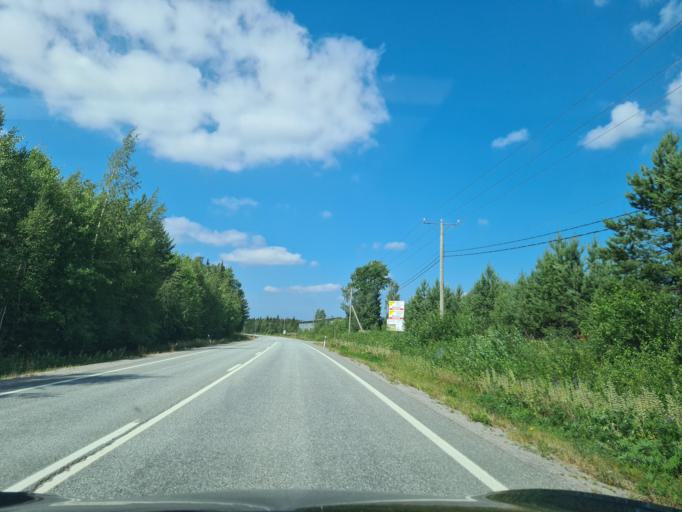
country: FI
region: Ostrobothnia
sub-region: Vaasa
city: Vaasa
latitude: 63.1662
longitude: 21.5891
